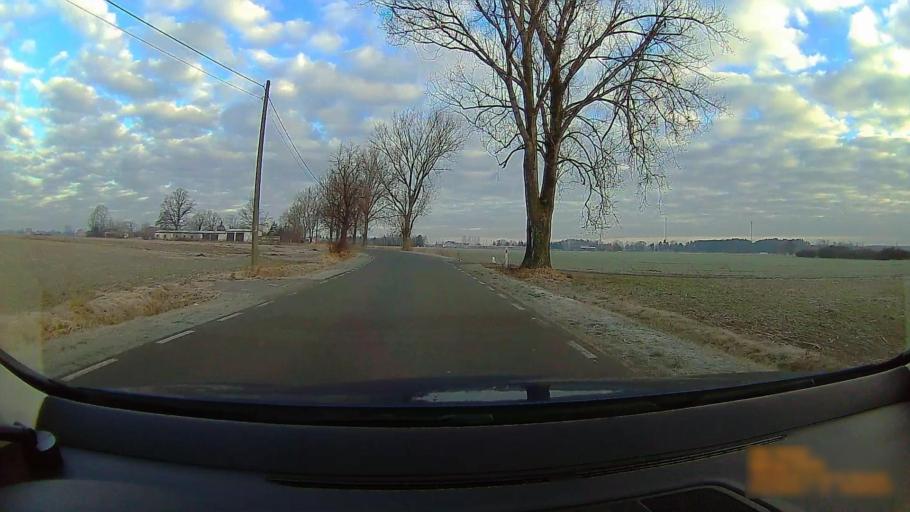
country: PL
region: Greater Poland Voivodeship
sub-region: Powiat koninski
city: Rzgow Pierwszy
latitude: 52.1465
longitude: 18.0554
